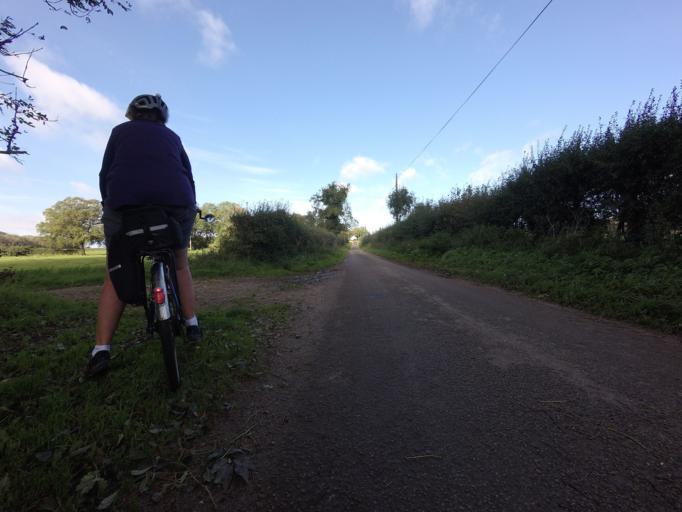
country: GB
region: England
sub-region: Norfolk
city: Dersingham
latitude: 52.8511
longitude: 0.6696
